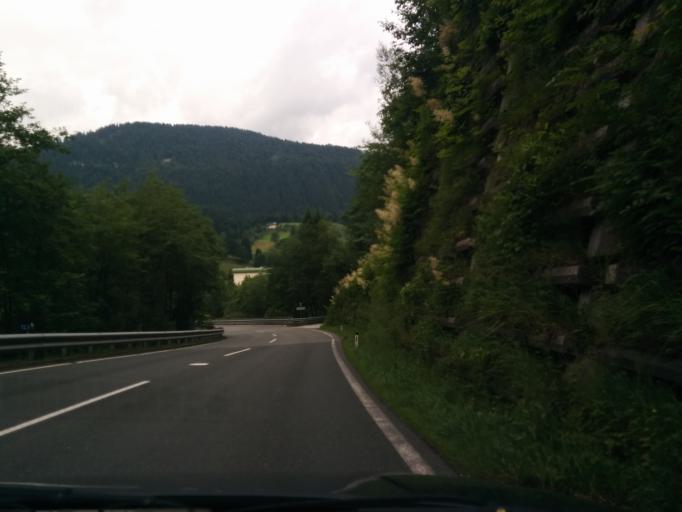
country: AT
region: Salzburg
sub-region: Politischer Bezirk Hallein
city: Abtenau
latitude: 47.5914
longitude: 13.3148
